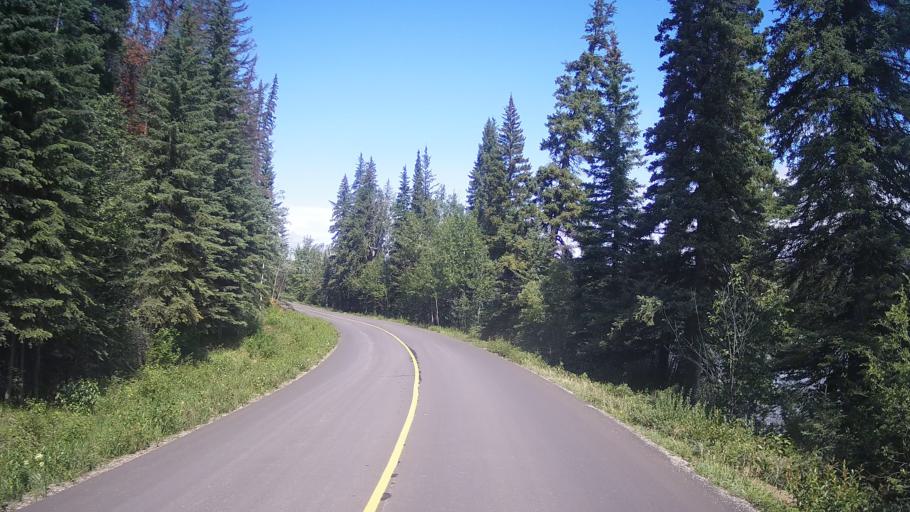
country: CA
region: Alberta
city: Jasper Park Lodge
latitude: 52.7384
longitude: -117.9585
